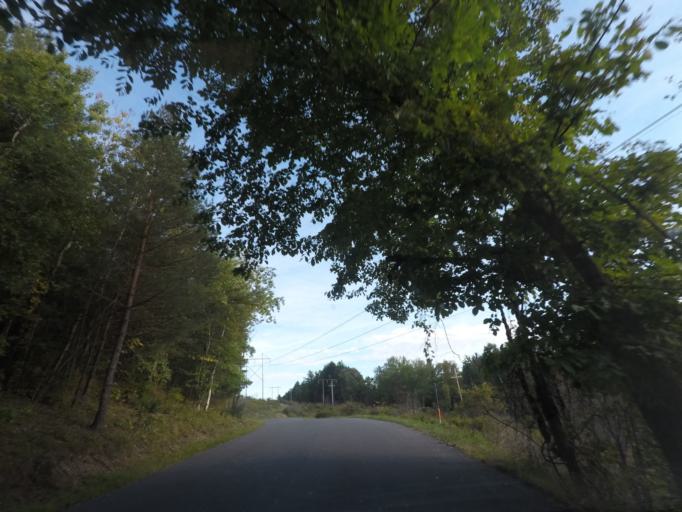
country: US
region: New York
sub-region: Rensselaer County
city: West Sand Lake
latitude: 42.6410
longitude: -73.6187
